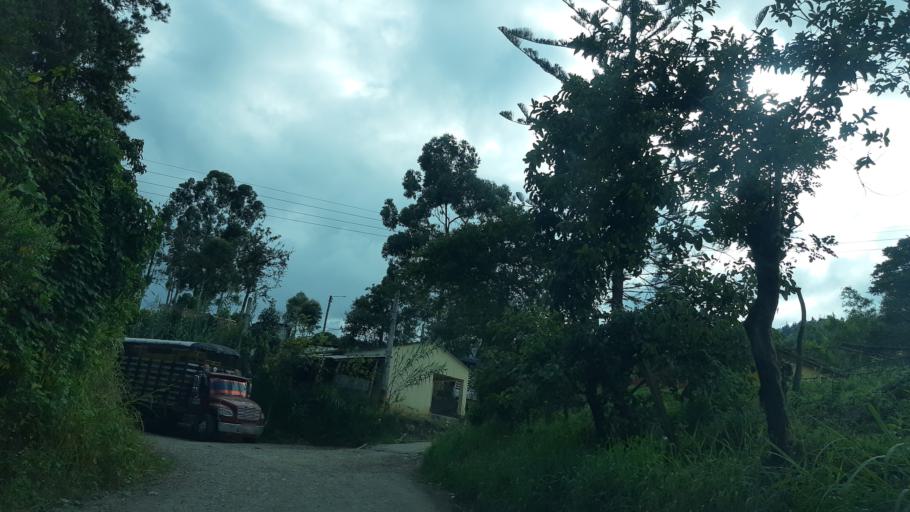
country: CO
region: Cundinamarca
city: Tenza
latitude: 5.0622
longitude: -73.4231
